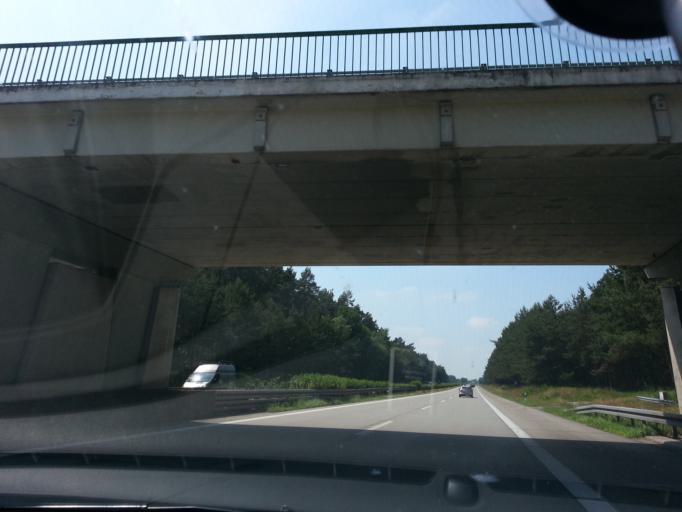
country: DE
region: Brandenburg
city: Heiligengrabe
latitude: 53.1705
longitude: 12.3485
